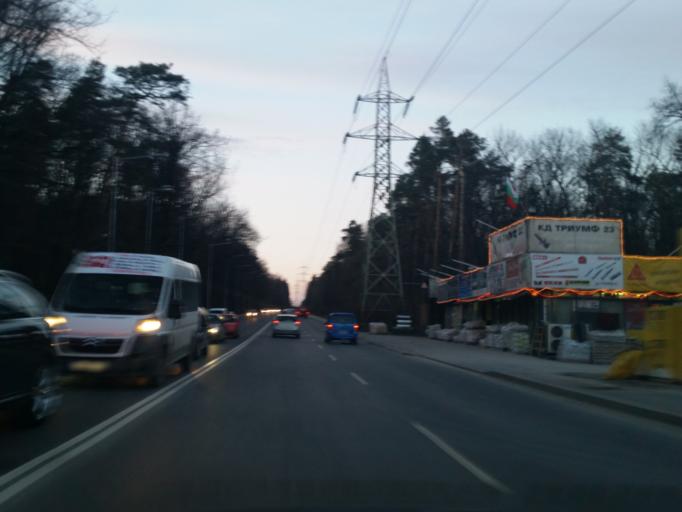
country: BG
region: Sofia-Capital
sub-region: Stolichna Obshtina
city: Sofia
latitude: 42.6670
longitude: 23.3376
